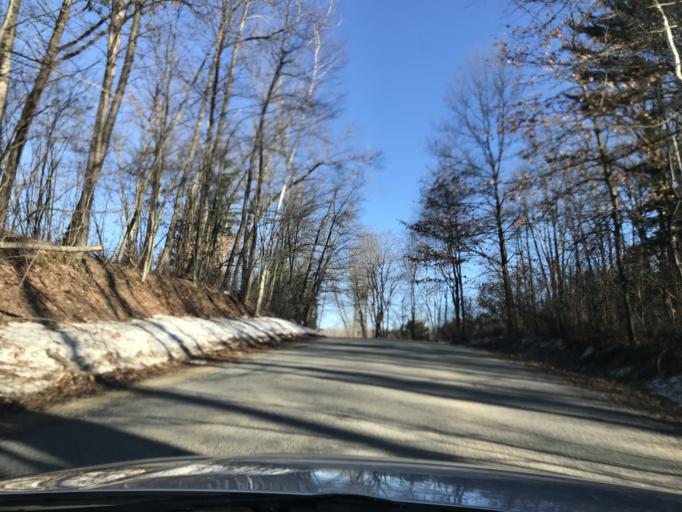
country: US
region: Wisconsin
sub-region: Marinette County
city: Niagara
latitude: 45.3821
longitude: -88.0395
